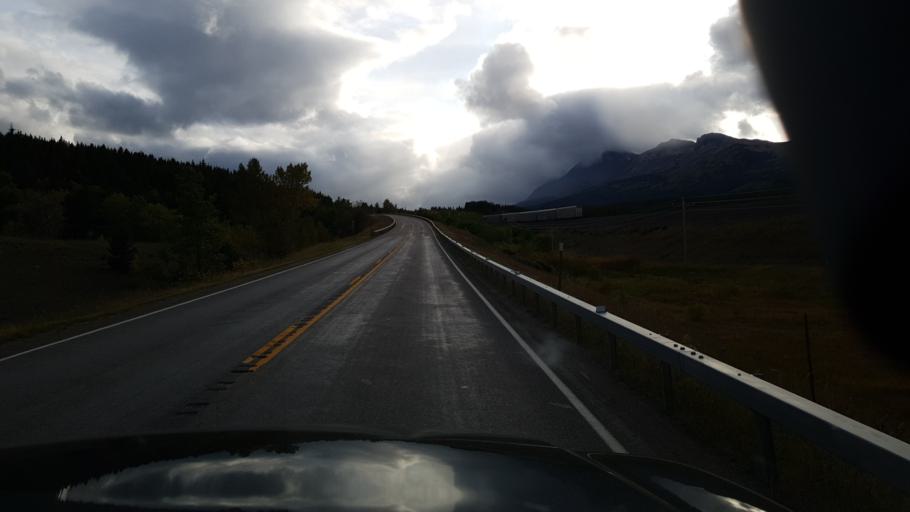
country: US
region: Montana
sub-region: Glacier County
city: South Browning
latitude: 48.3853
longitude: -113.2683
